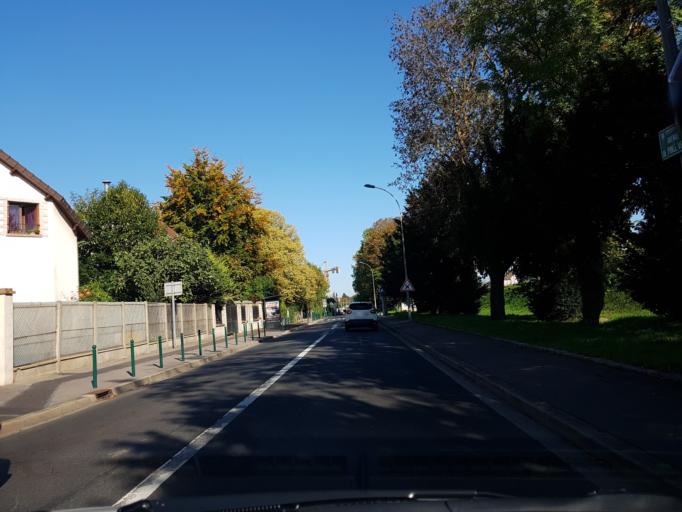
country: FR
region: Ile-de-France
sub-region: Departement du Val-de-Marne
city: Ormesson-sur-Marne
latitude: 48.7894
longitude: 2.5490
